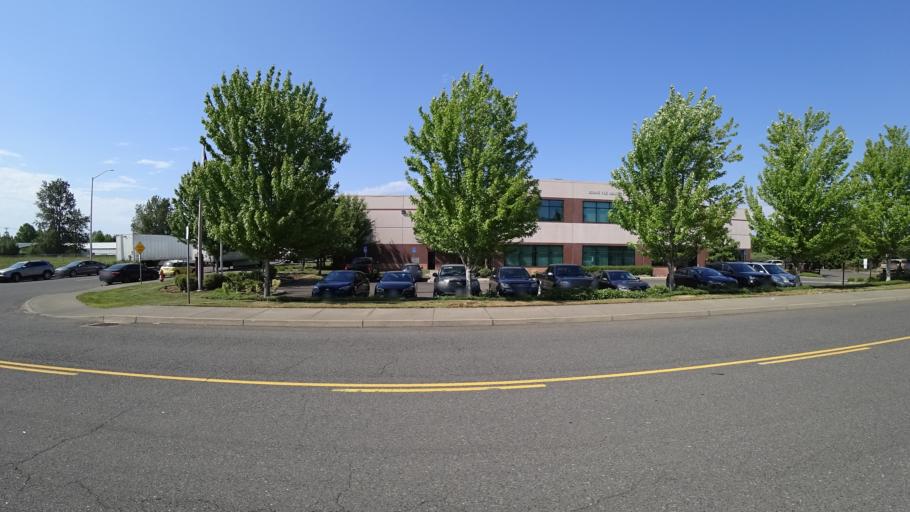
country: US
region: Oregon
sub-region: Multnomah County
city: Fairview
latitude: 45.5547
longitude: -122.5079
